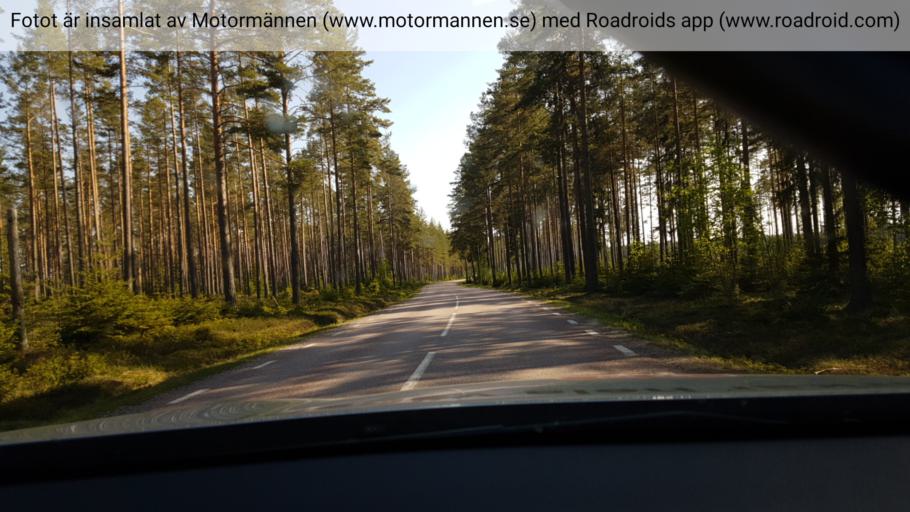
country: SE
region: Gaevleborg
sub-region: Sandvikens Kommun
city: Arsunda
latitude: 60.4869
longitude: 16.7213
